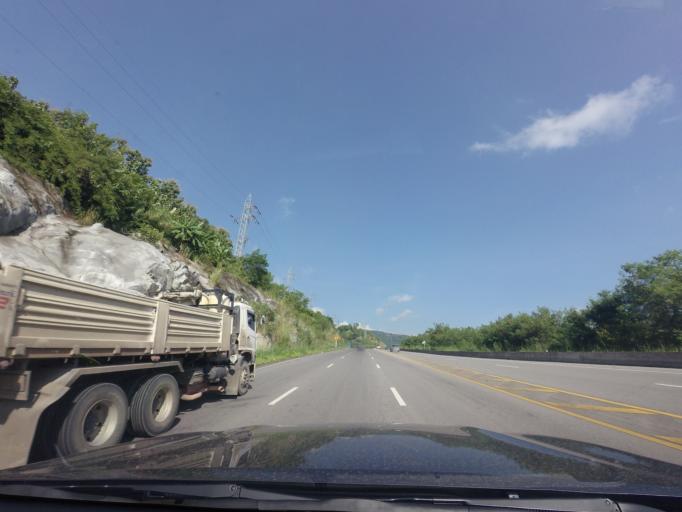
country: TH
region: Phetchabun
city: Lom Sak
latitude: 16.7747
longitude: 101.1208
